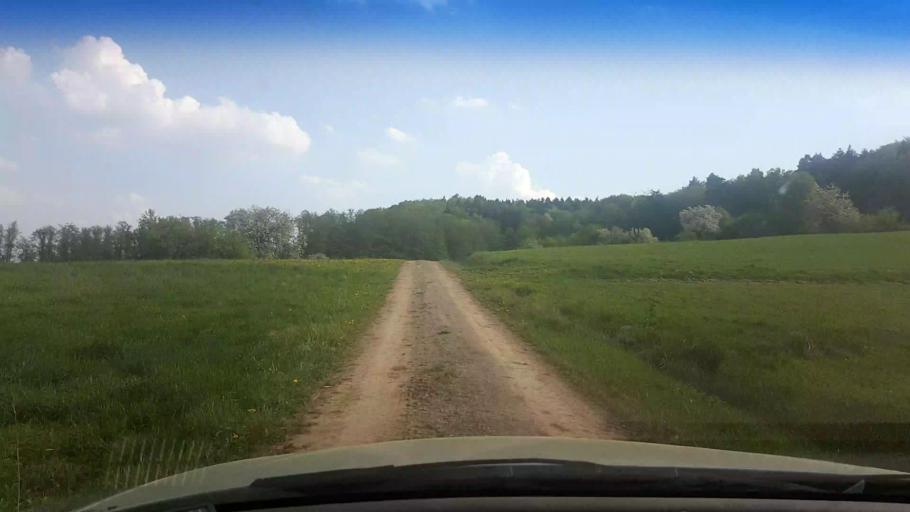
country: DE
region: Bavaria
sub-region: Upper Franconia
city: Rattelsdorf
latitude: 50.0129
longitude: 10.8683
